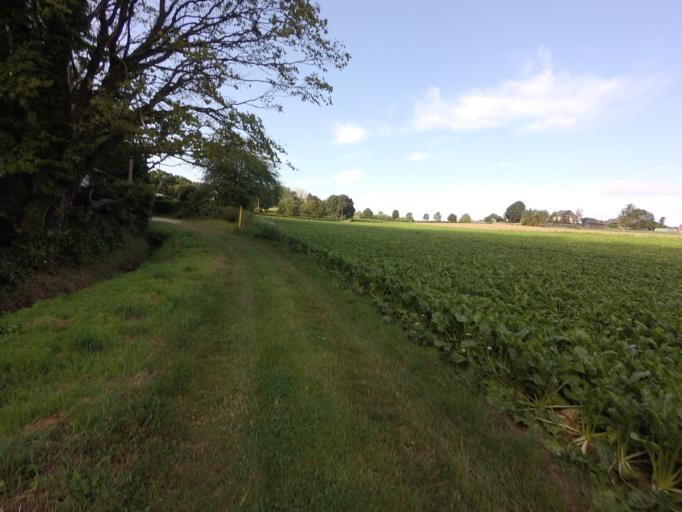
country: DE
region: North Rhine-Westphalia
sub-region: Regierungsbezirk Koln
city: Herzogenrath
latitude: 50.8593
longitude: 6.1330
